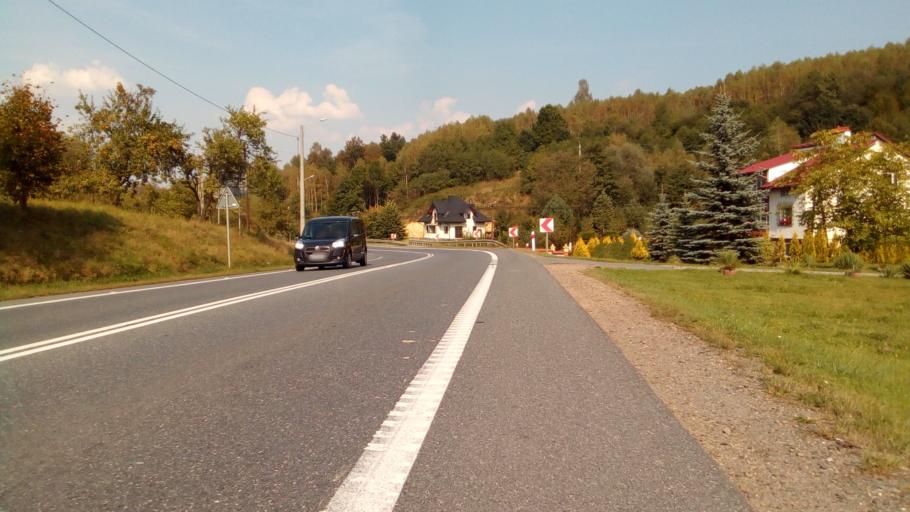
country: PL
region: Subcarpathian Voivodeship
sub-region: Powiat strzyzowski
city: Jawornik
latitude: 49.8475
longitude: 21.8952
